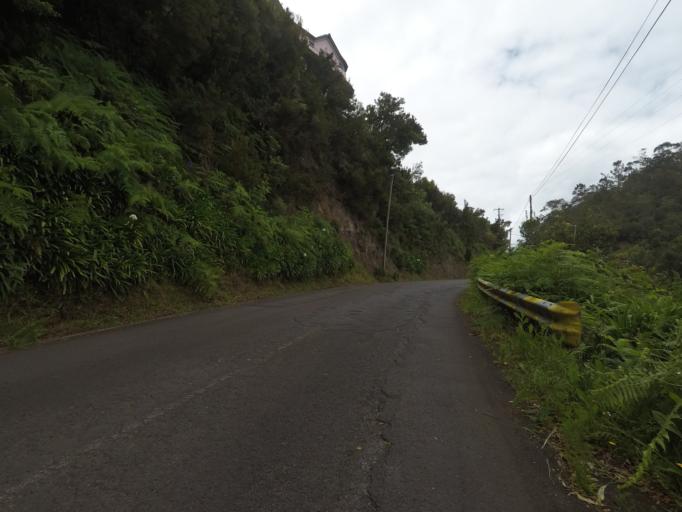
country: PT
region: Madeira
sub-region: Santana
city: Santana
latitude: 32.7957
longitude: -16.8656
